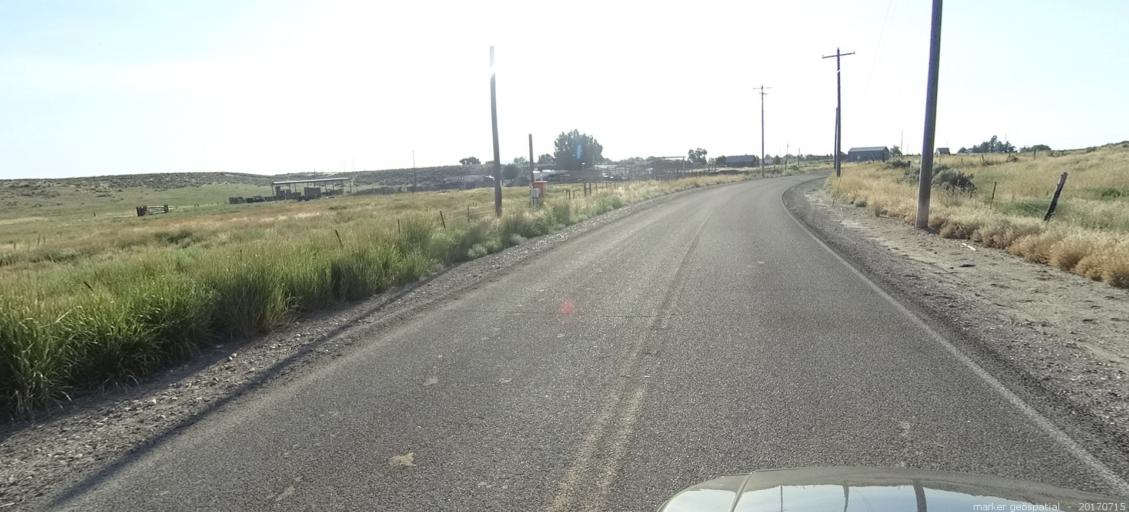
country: US
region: Idaho
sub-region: Ada County
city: Boise
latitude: 43.3894
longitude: -115.9763
